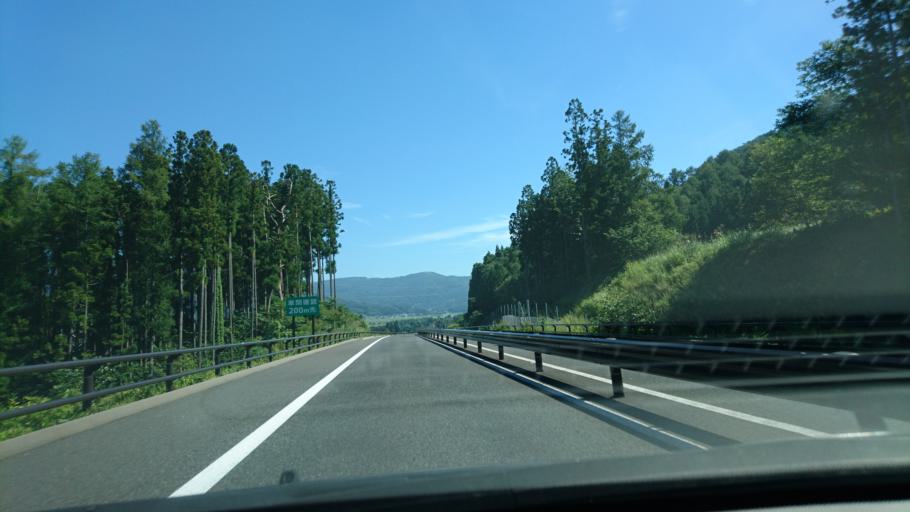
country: JP
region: Iwate
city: Tono
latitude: 39.3090
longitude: 141.4424
